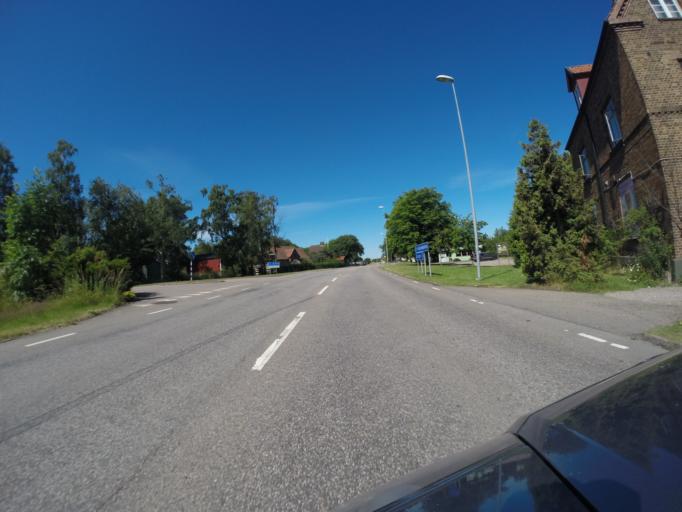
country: SE
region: Skane
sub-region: Helsingborg
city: Hyllinge
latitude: 56.1020
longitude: 12.8678
